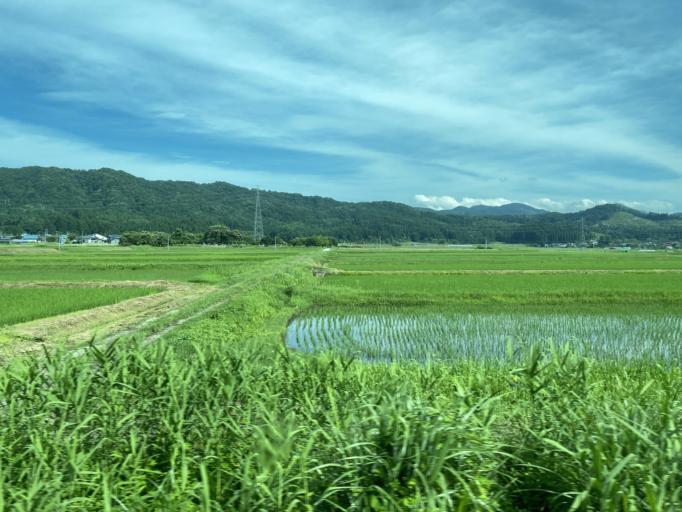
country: JP
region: Fukushima
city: Kitakata
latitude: 37.5973
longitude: 139.6627
